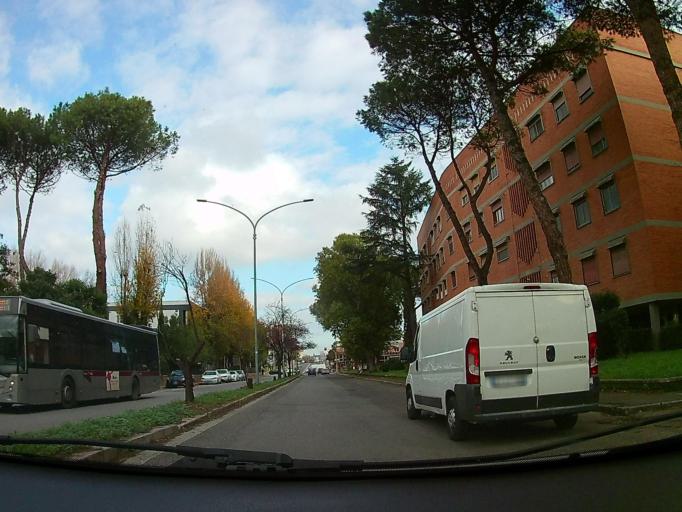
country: IT
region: Latium
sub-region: Citta metropolitana di Roma Capitale
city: Vitinia
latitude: 41.8201
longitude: 12.4426
